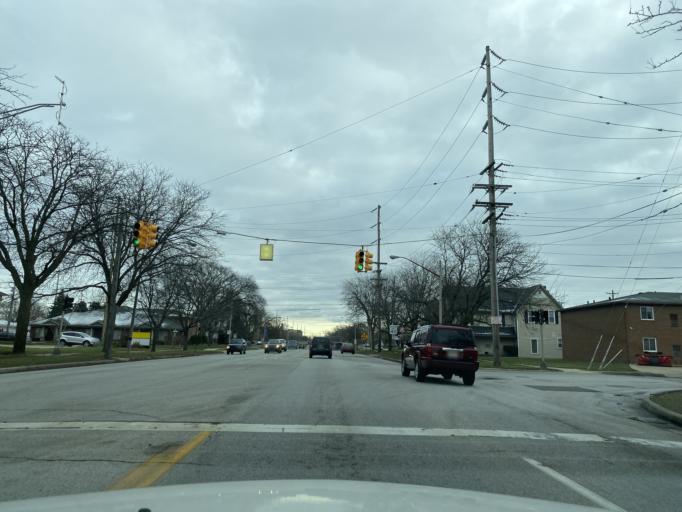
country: US
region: Michigan
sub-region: Wayne County
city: Wyandotte
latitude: 42.1997
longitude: -83.1668
